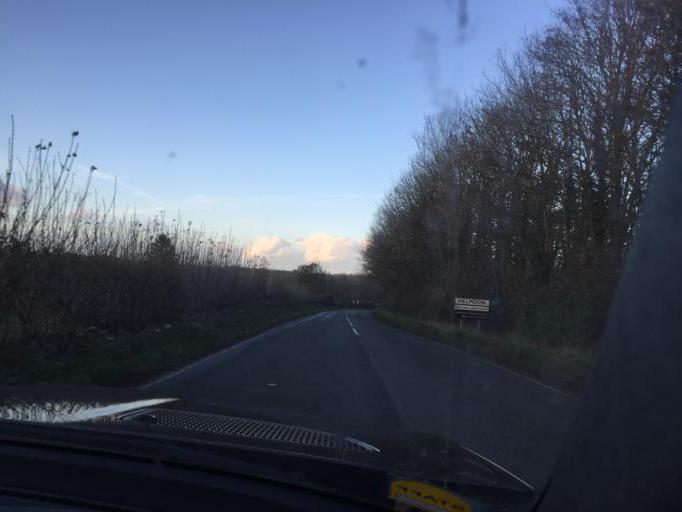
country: GB
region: England
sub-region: Northamptonshire
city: Brackley
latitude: 52.0811
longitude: -1.1463
